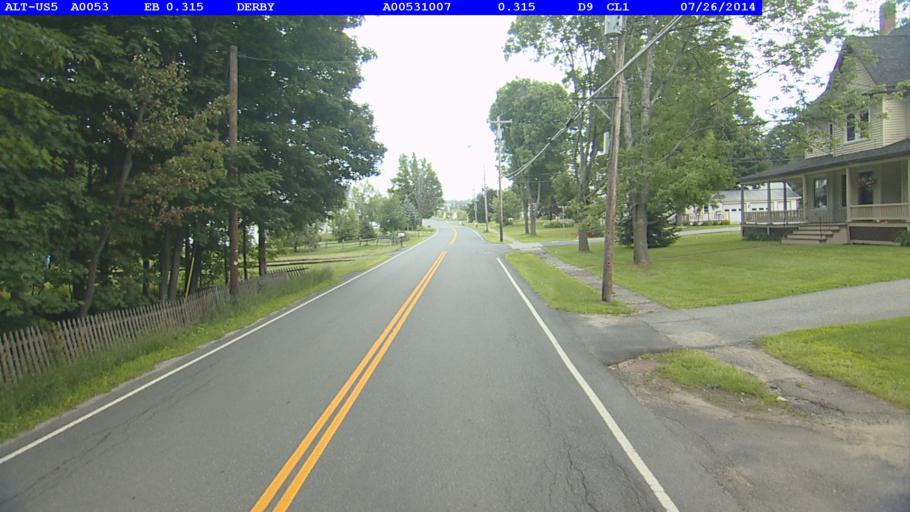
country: US
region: Vermont
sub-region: Orleans County
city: Newport
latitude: 45.0053
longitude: -72.0934
